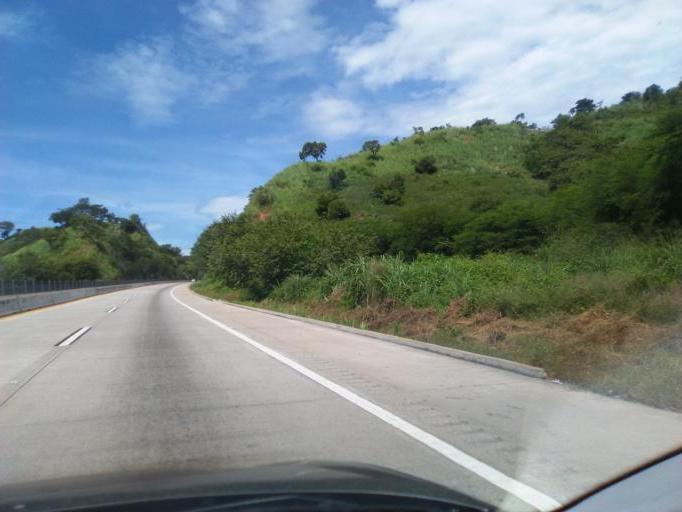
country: MX
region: Guerrero
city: Tierra Colorada
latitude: 17.1471
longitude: -99.5538
